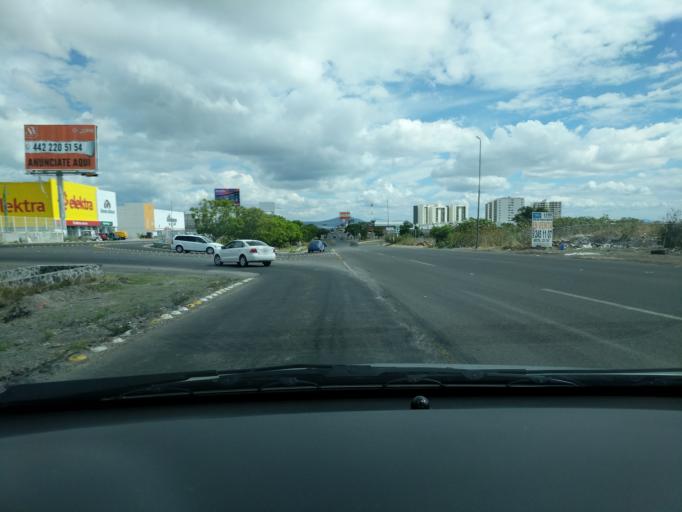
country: MX
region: Queretaro
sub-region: El Marques
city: La Pradera
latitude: 20.6571
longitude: -100.3433
